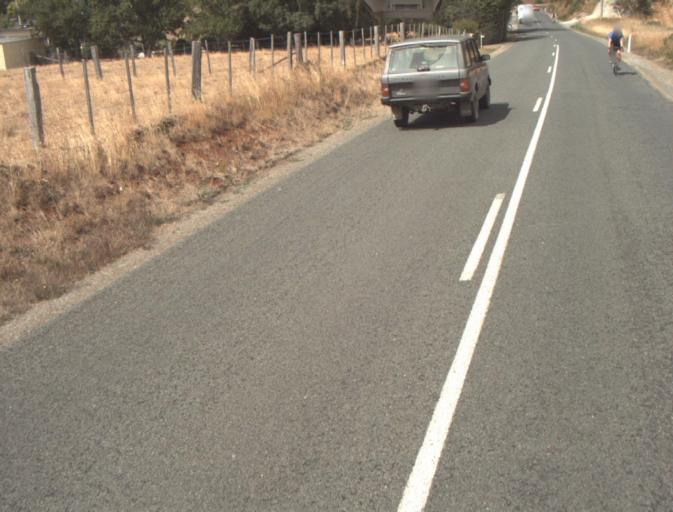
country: AU
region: Tasmania
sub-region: Launceston
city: Mayfield
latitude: -41.1889
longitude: 147.2217
